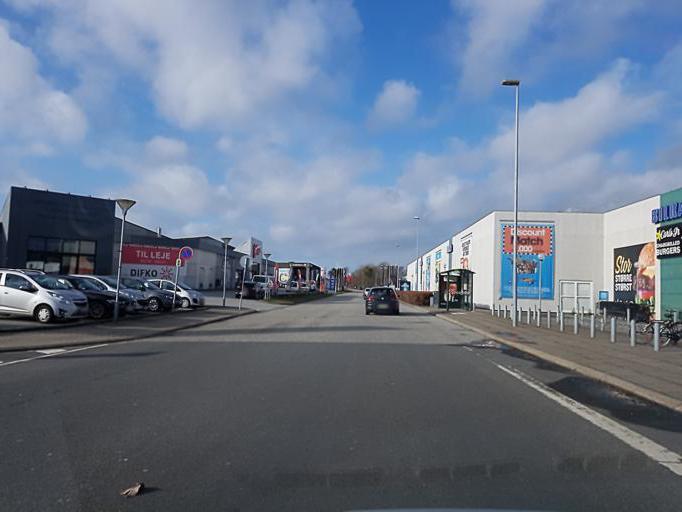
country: DK
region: Central Jutland
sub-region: Holstebro Kommune
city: Holstebro
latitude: 56.3771
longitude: 8.6210
